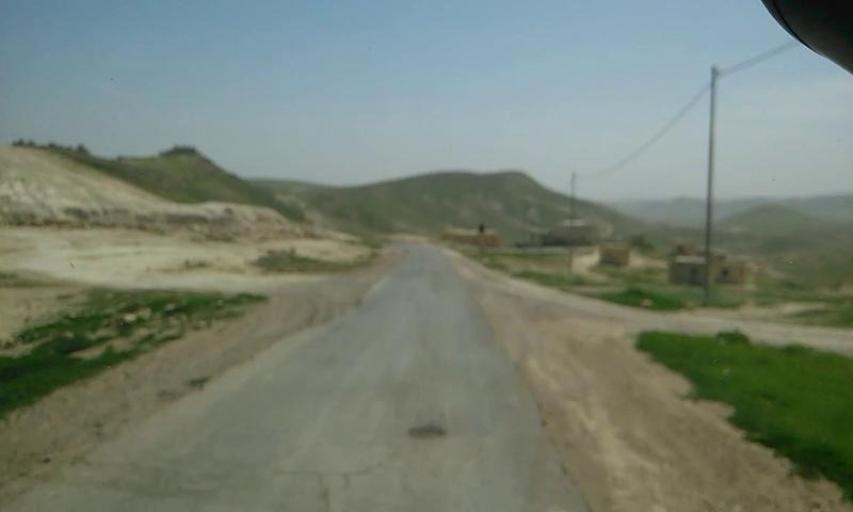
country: PS
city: `Arab ar Rashaydah
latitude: 31.5663
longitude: 35.2379
